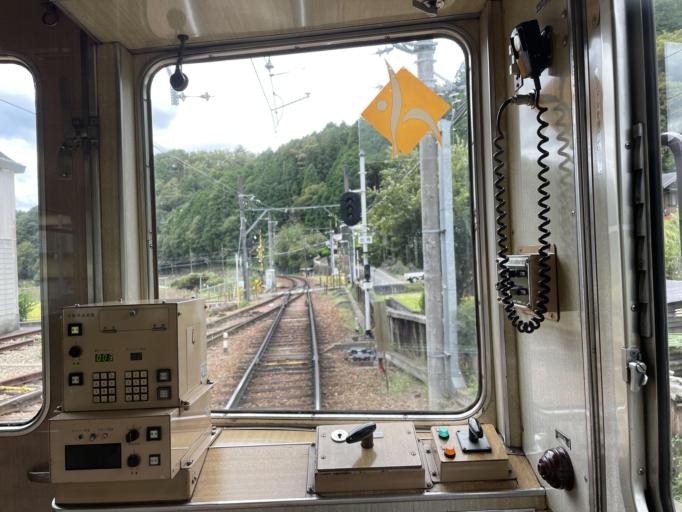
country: JP
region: Osaka
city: Mino
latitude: 34.9113
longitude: 135.4442
